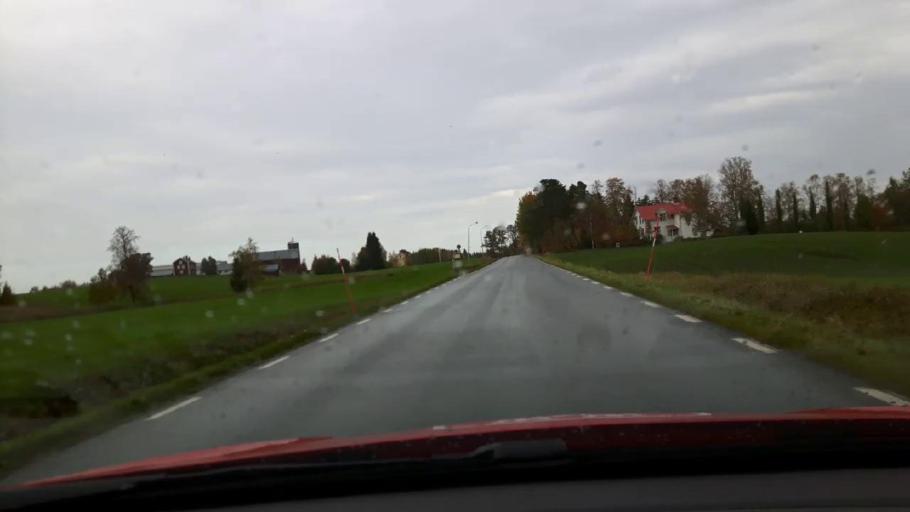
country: SE
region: Jaemtland
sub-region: Bergs Kommun
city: Hoverberg
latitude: 63.0334
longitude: 14.3453
